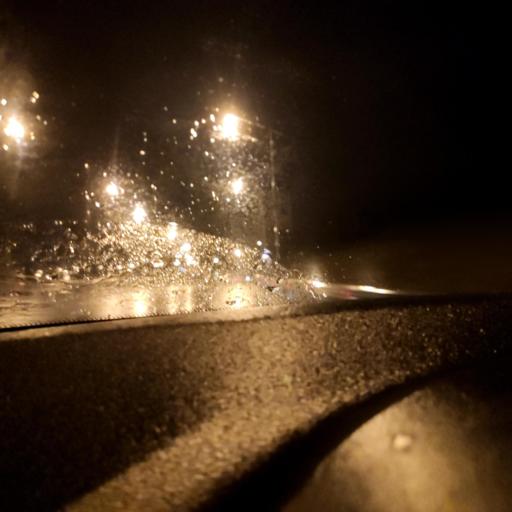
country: RU
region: Samara
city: Volzhskiy
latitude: 53.3684
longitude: 50.1929
